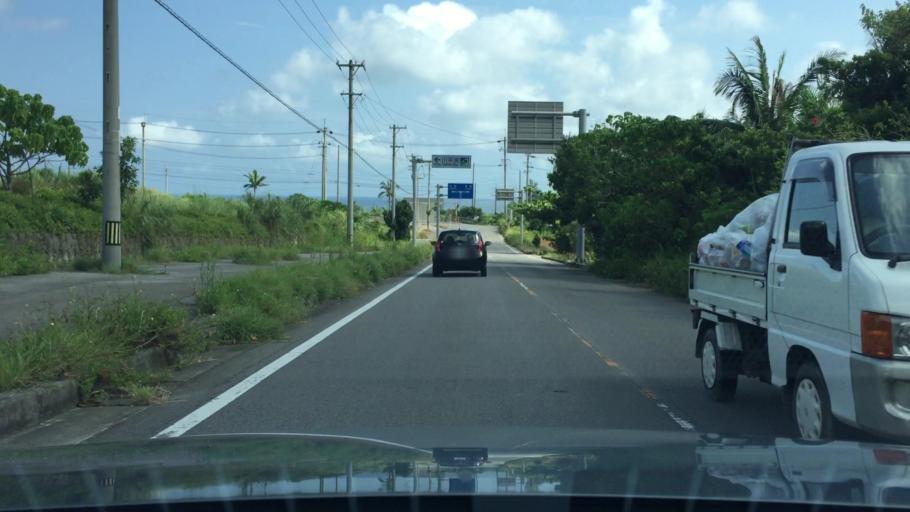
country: JP
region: Okinawa
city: Ishigaki
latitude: 24.4524
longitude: 124.2059
